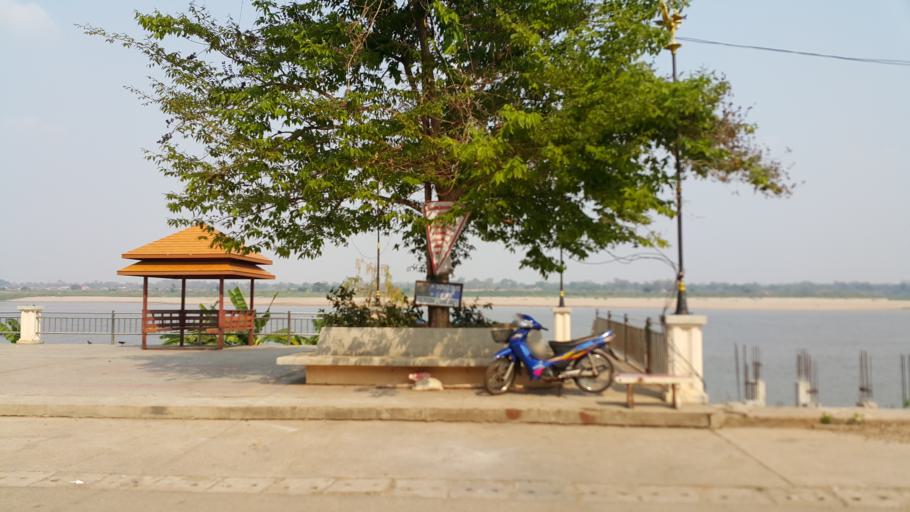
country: TH
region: Nakhon Phanom
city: That Phanom
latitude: 16.9434
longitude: 104.7294
